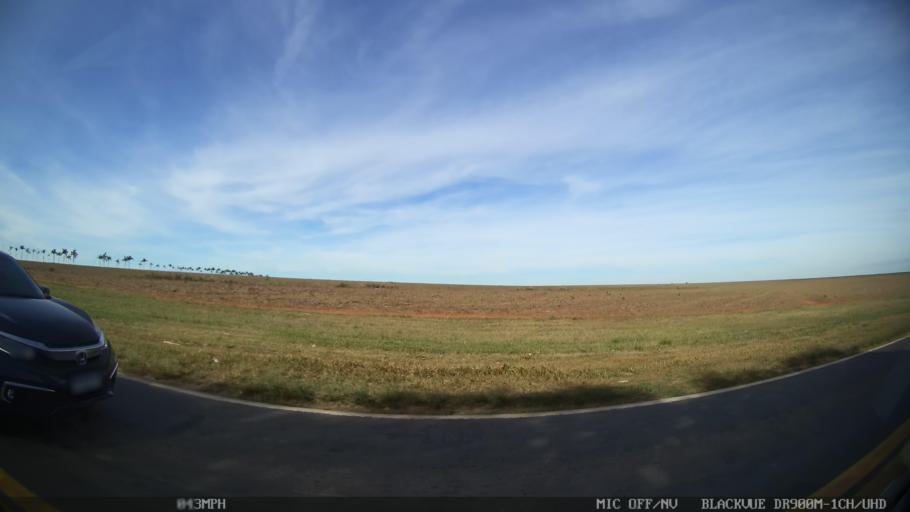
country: BR
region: Sao Paulo
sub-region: Rio Das Pedras
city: Rio das Pedras
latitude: -22.7952
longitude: -47.5907
